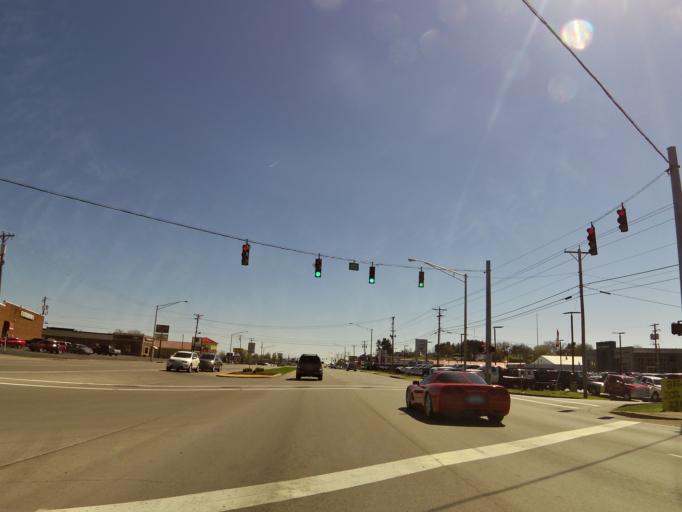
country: US
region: Kentucky
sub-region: Pulaski County
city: Somerset
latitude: 37.0796
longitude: -84.6175
